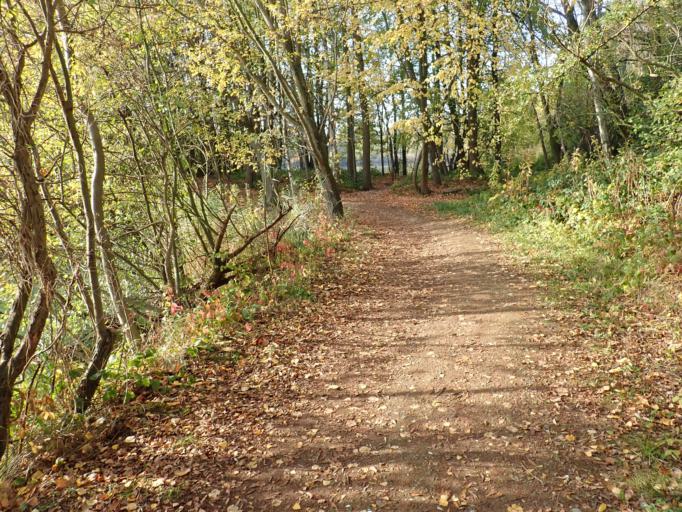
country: BE
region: Flanders
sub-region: Provincie Antwerpen
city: Niel
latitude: 51.1070
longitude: 4.3482
